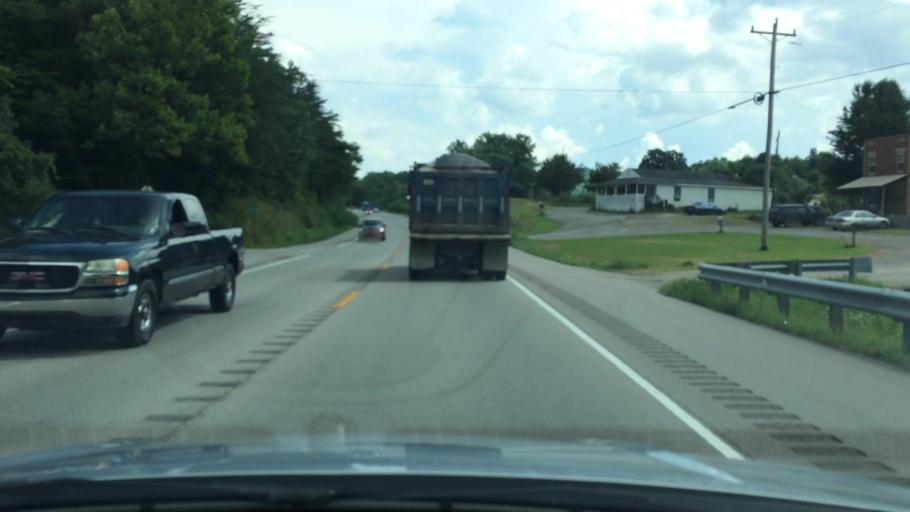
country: US
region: Kentucky
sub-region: McCreary County
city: Whitley City
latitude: 36.8768
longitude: -84.4952
